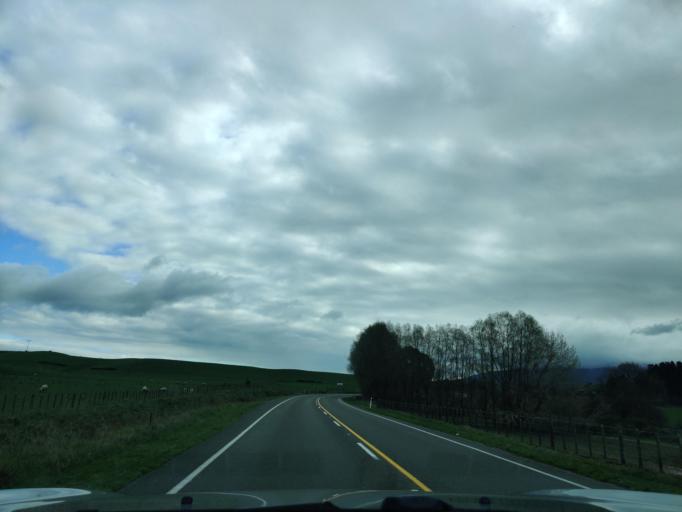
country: NZ
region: Manawatu-Wanganui
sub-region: Palmerston North City
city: Palmerston North
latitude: -40.2827
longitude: 175.9812
